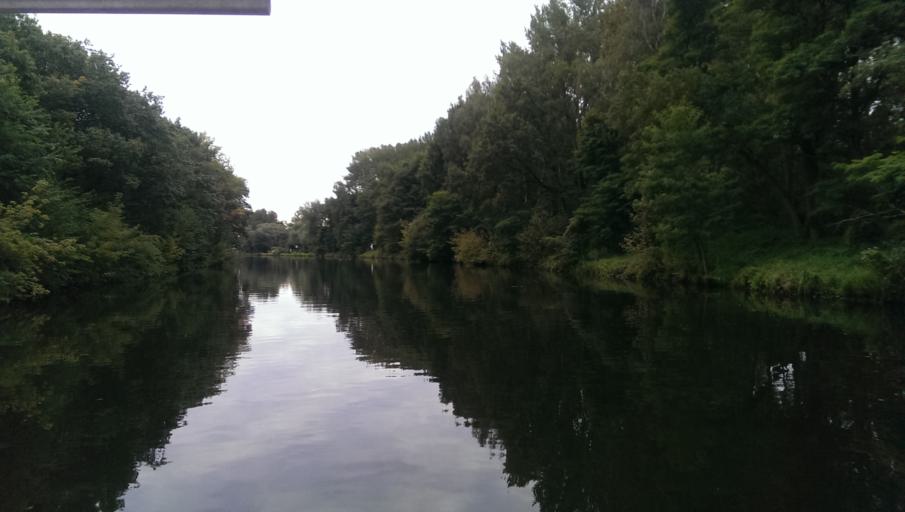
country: DE
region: Brandenburg
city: Oranienburg
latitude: 52.7118
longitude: 13.2452
